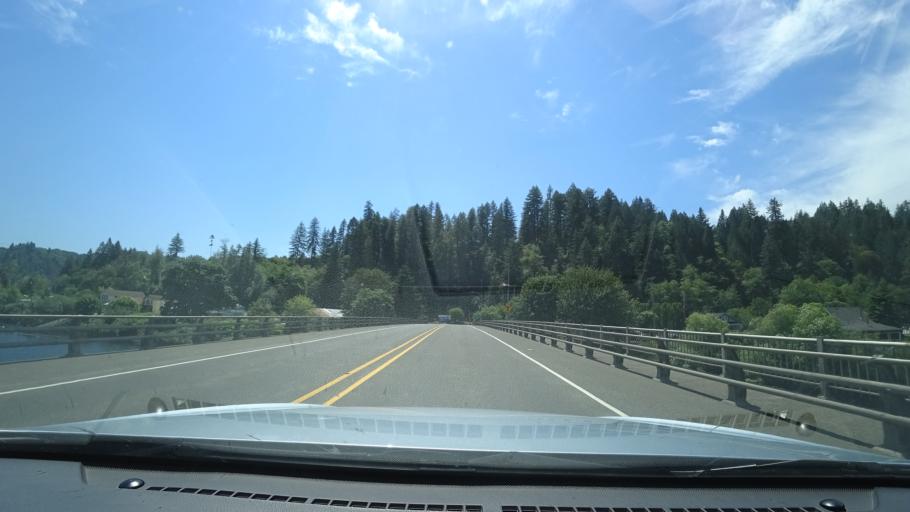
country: US
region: Oregon
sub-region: Lane County
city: Florence
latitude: 44.0321
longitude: -123.8577
